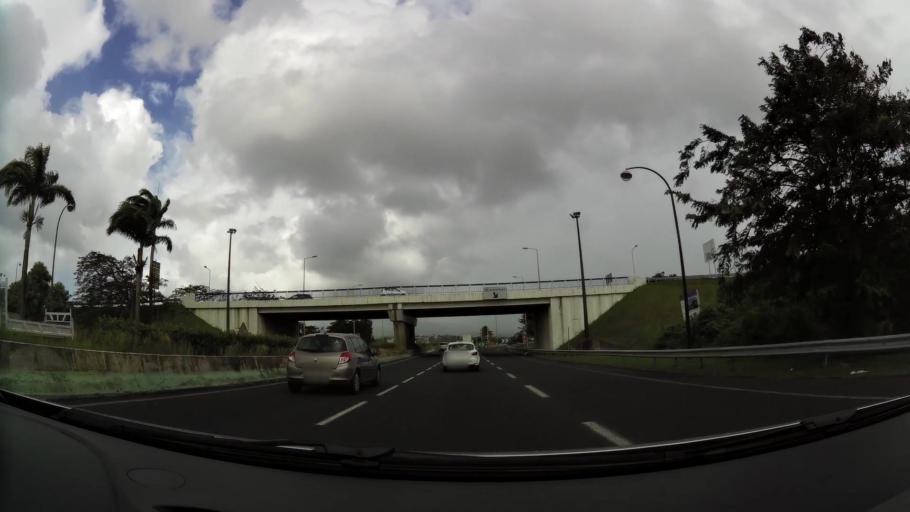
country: MQ
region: Martinique
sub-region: Martinique
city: Le Lamentin
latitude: 14.5987
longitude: -60.9992
